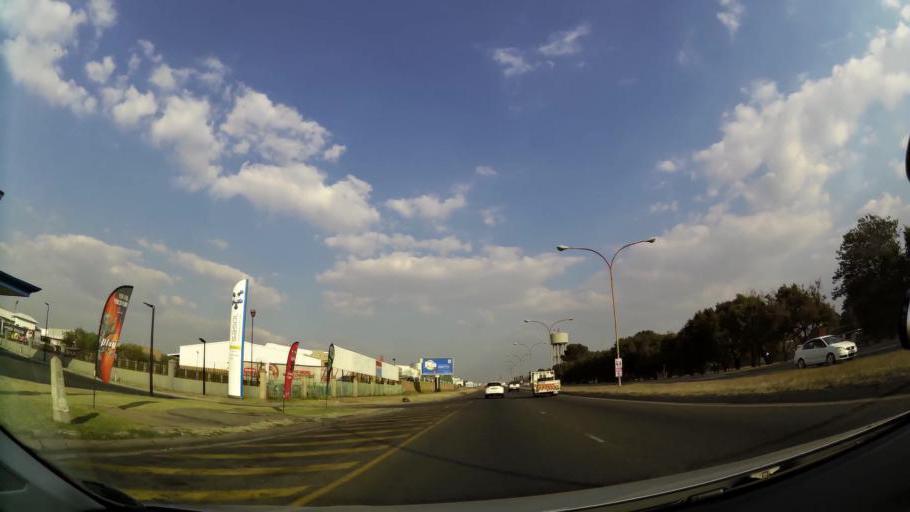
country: ZA
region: Gauteng
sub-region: City of Johannesburg Metropolitan Municipality
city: Modderfontein
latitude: -26.1185
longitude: 28.1998
